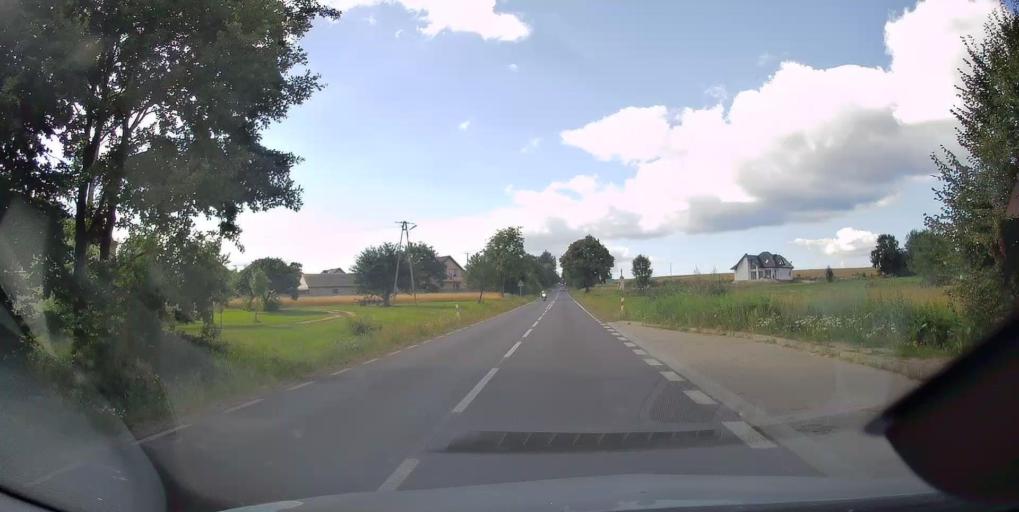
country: PL
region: Swietokrzyskie
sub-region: Powiat kielecki
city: Bodzentyn
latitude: 50.9180
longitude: 20.9927
